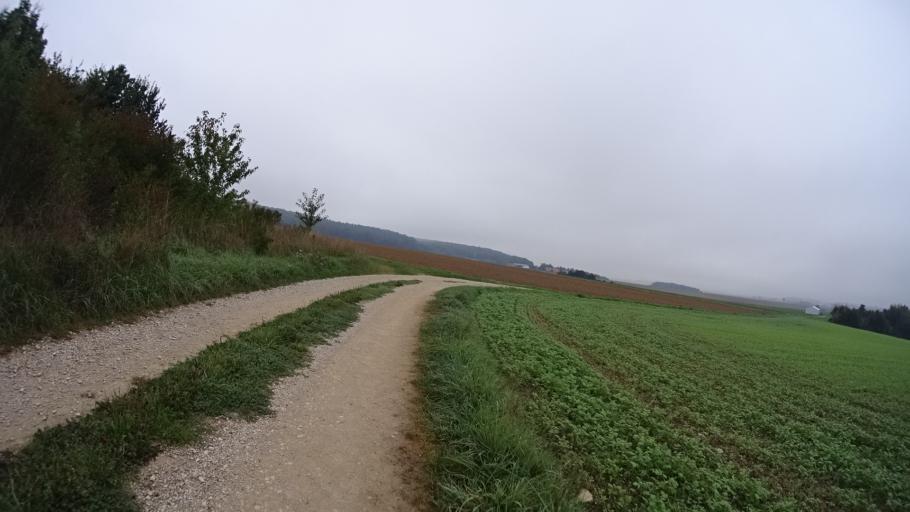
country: DE
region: Bavaria
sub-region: Upper Bavaria
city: Hepberg
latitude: 48.8265
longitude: 11.4775
